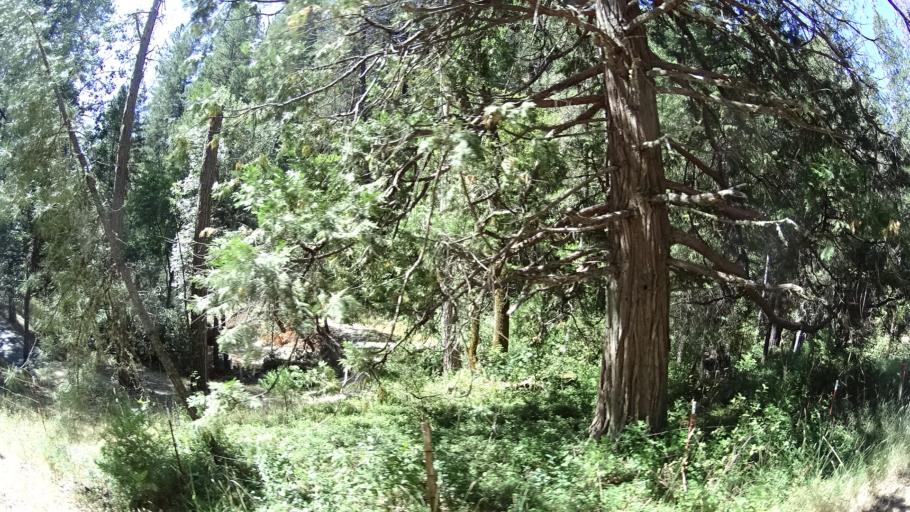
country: US
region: California
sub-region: Amador County
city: Pioneer
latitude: 38.3871
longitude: -120.4995
